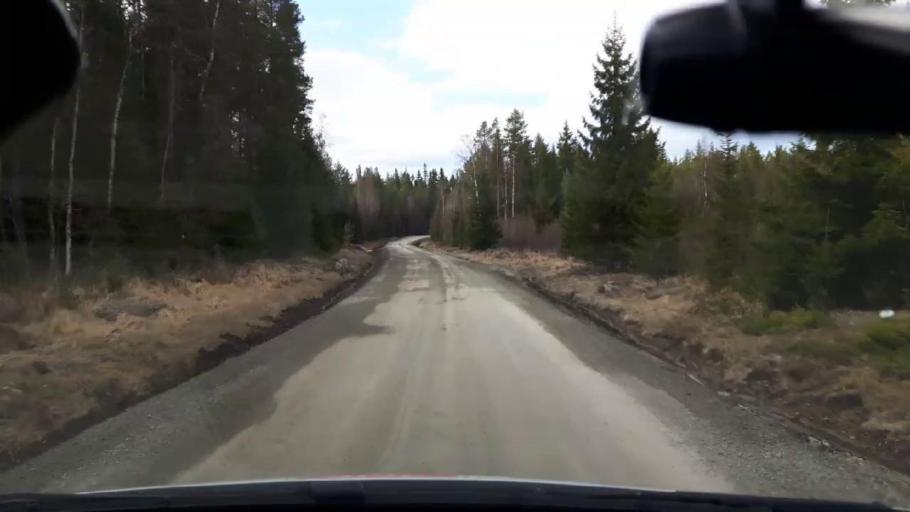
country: SE
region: Jaemtland
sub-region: Bergs Kommun
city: Hoverberg
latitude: 62.9063
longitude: 14.6366
